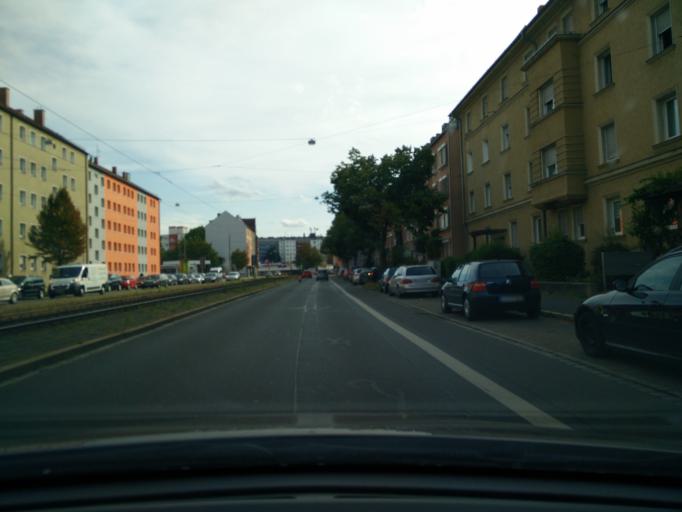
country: DE
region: Bavaria
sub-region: Regierungsbezirk Mittelfranken
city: Nuernberg
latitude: 49.4309
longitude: 11.0665
